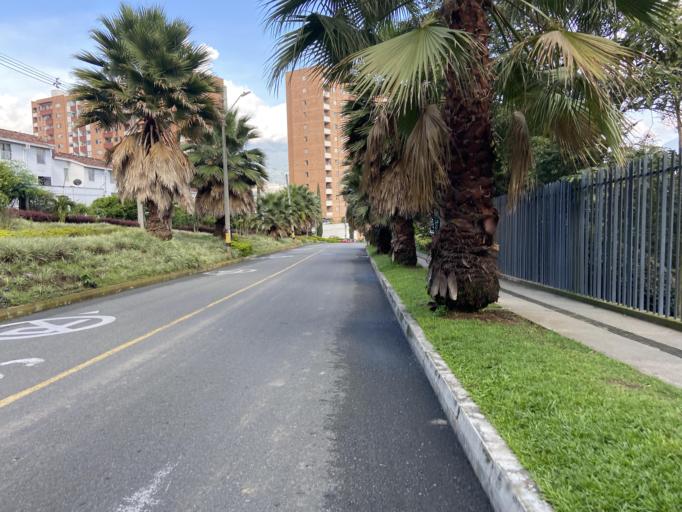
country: CO
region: Antioquia
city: Sabaneta
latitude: 6.1543
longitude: -75.6055
